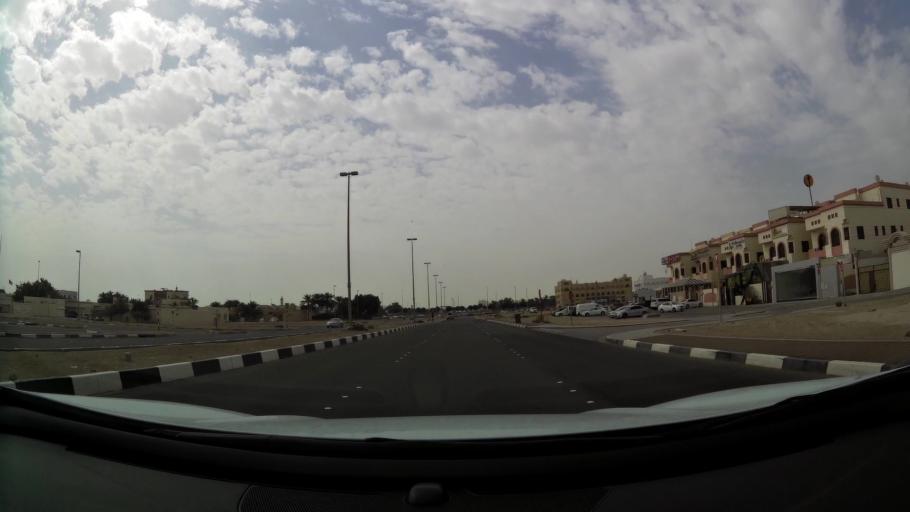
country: AE
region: Abu Dhabi
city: Abu Dhabi
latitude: 24.2980
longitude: 54.6311
